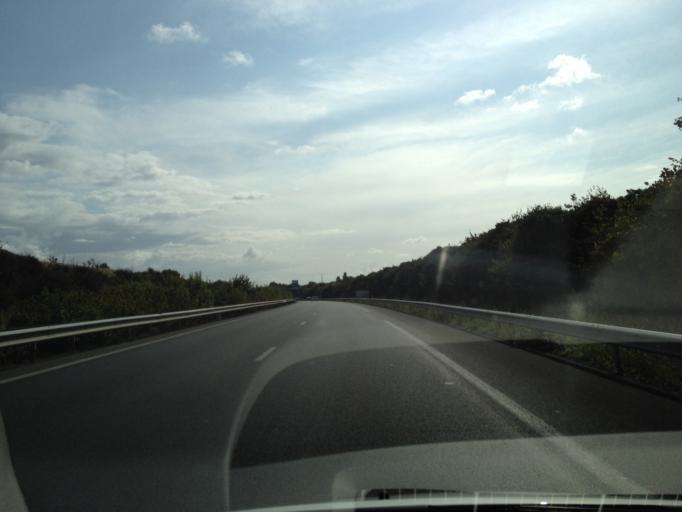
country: FR
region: Poitou-Charentes
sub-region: Departement de la Charente-Maritime
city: Sainte-Soulle
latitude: 46.1995
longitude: -1.0349
